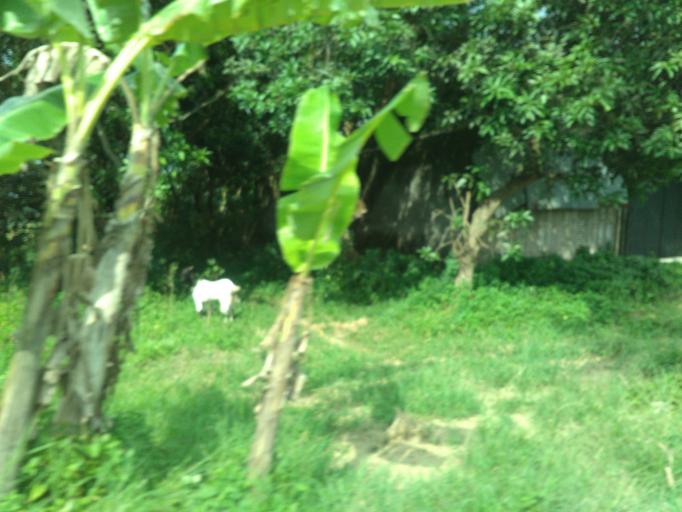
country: ID
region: Central Java
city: Delanggu
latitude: -7.6300
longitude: 110.6921
